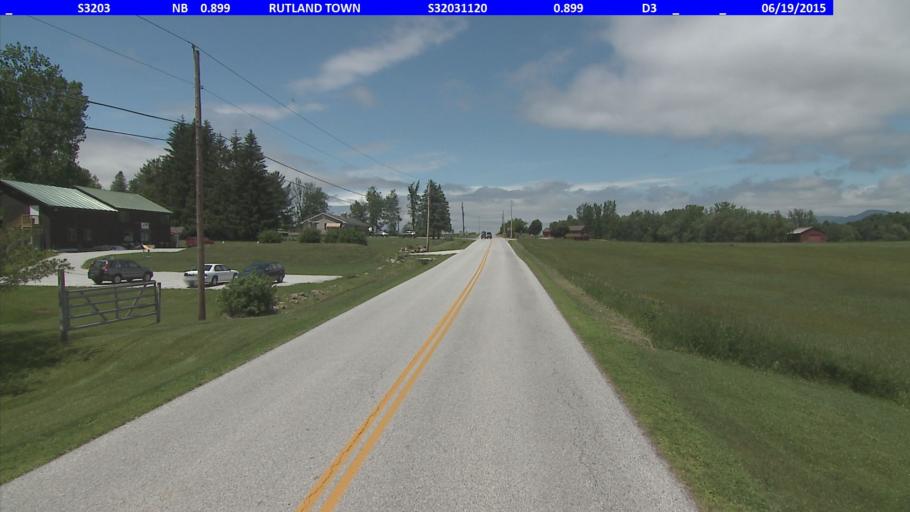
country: US
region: Vermont
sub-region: Rutland County
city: Rutland
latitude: 43.6655
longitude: -73.0020
